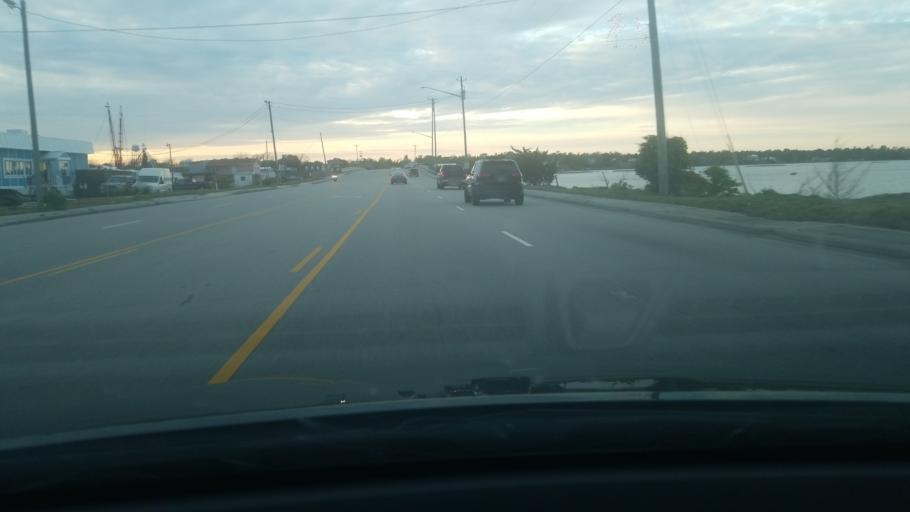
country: US
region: North Carolina
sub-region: Onslow County
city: Swansboro
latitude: 34.6847
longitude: -77.1145
